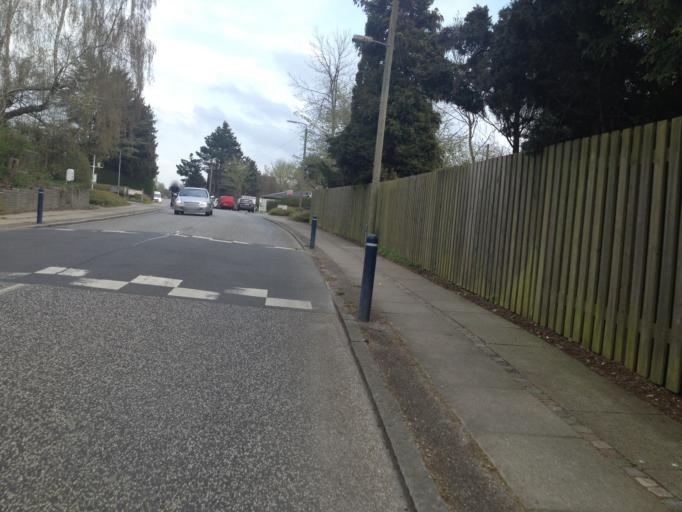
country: DK
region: Capital Region
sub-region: Ballerup Kommune
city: Ballerup
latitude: 55.7507
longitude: 12.3856
